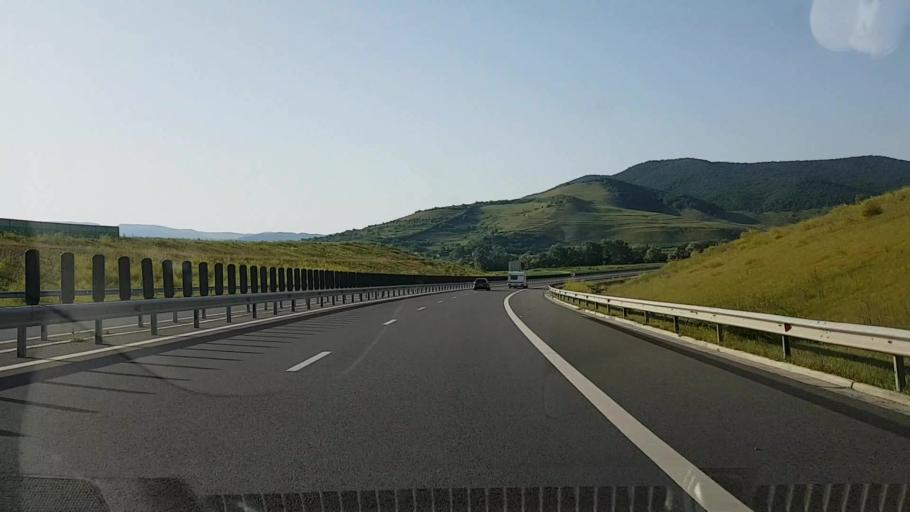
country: RO
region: Alba
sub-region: Comuna Miraslau
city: Miraslau
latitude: 46.3499
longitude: 23.7247
